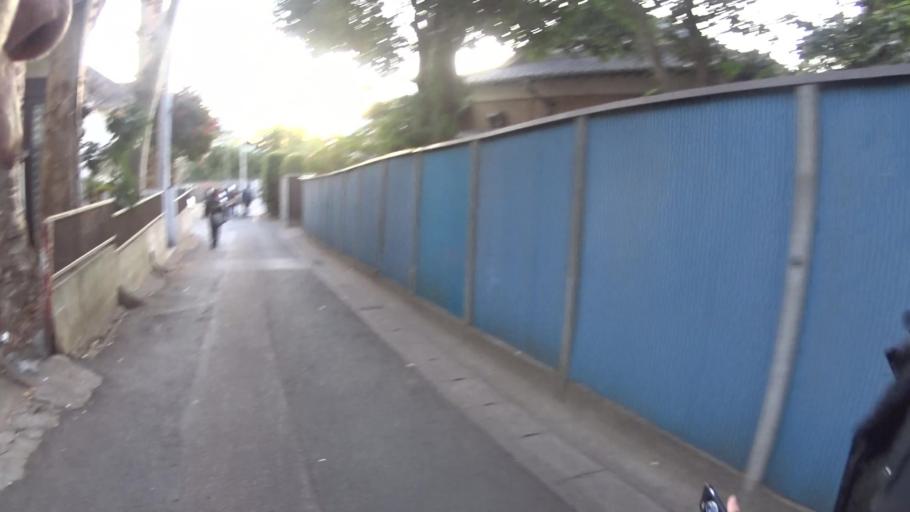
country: JP
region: Saitama
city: Shimotoda
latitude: 35.8461
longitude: 139.6799
